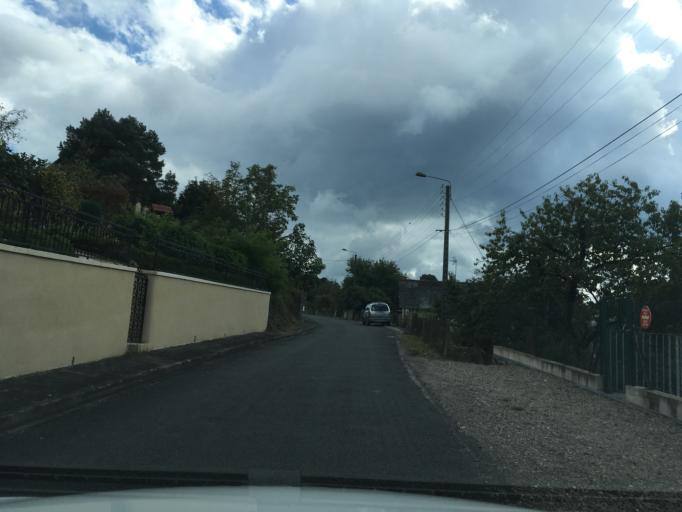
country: FR
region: Limousin
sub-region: Departement de la Correze
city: Brive-la-Gaillarde
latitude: 45.1473
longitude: 1.5374
